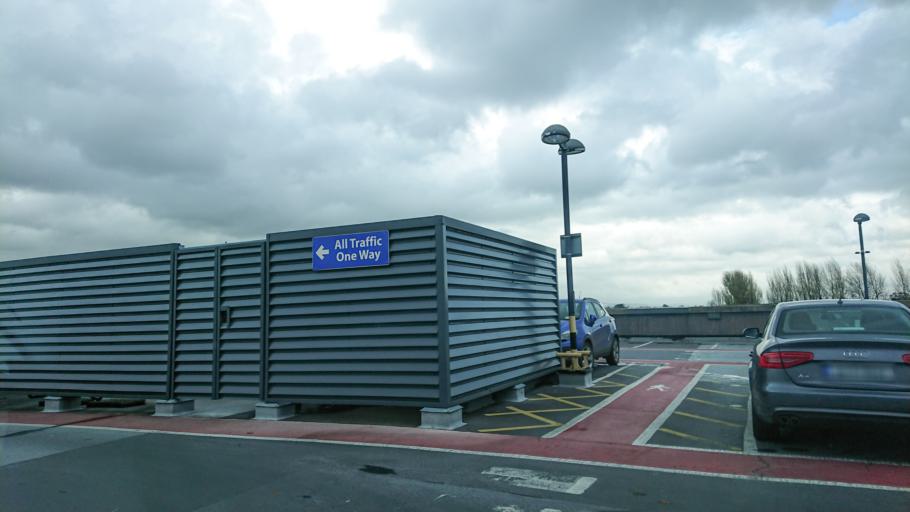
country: IE
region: Munster
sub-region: South Tipperary
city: Cluain Meala
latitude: 52.3548
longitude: -7.6911
